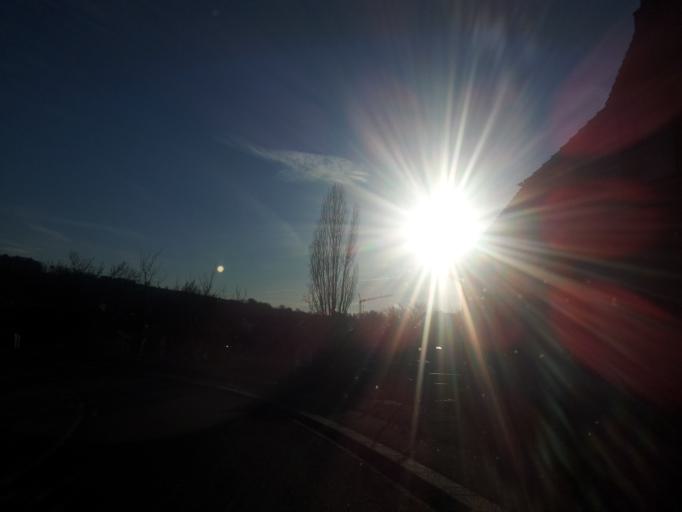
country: DE
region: Baden-Wuerttemberg
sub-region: Regierungsbezirk Stuttgart
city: Flein
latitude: 49.1056
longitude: 9.2111
